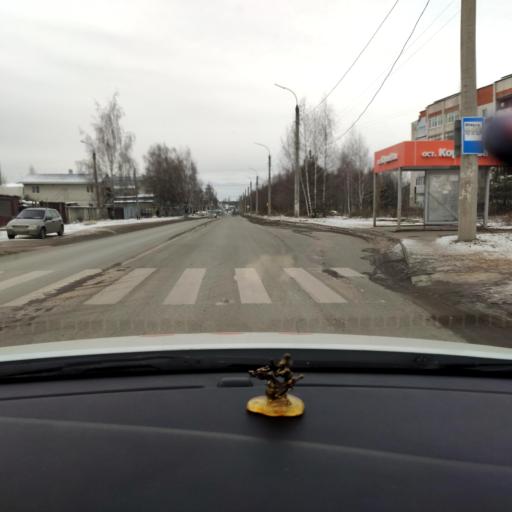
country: RU
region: Tatarstan
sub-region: Zelenodol'skiy Rayon
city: Zelenodolsk
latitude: 55.8625
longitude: 48.5501
